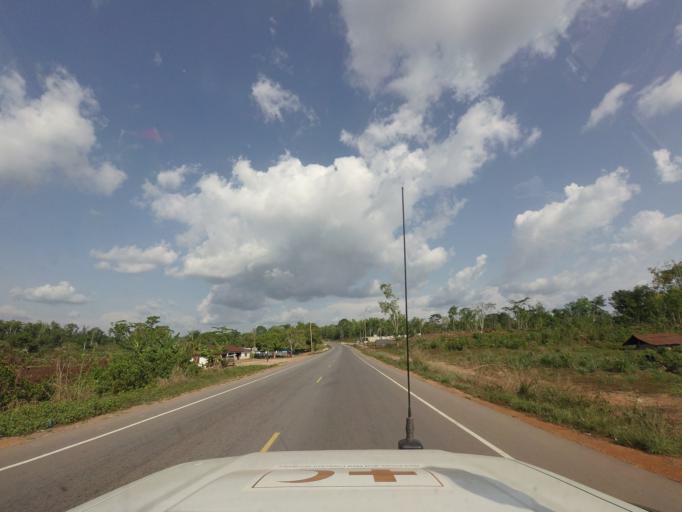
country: LR
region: Bong
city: Gbarnga
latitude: 6.8865
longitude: -9.6735
